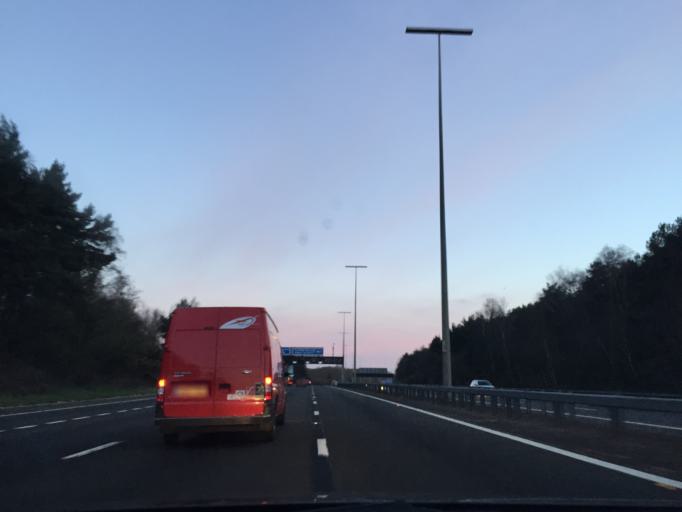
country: GB
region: England
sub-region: Hampshire
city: Hedge End
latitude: 50.9066
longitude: -1.3171
